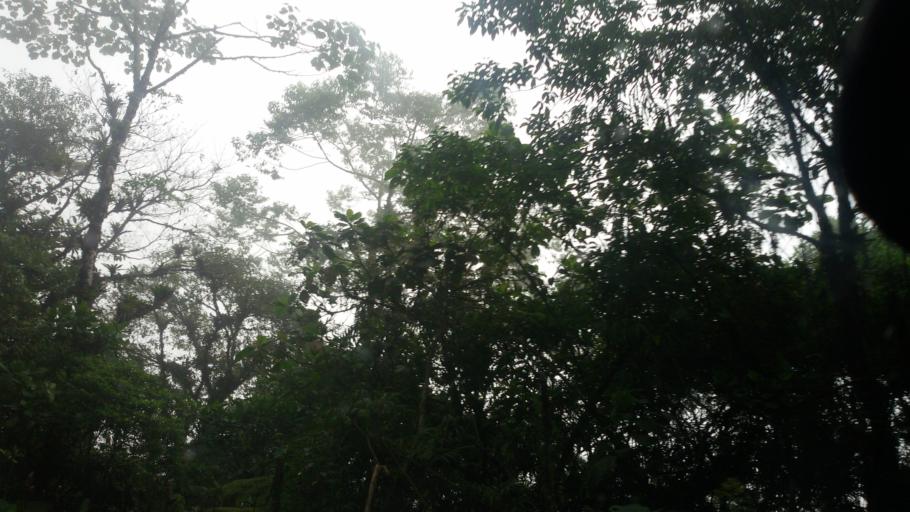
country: CR
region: San Jose
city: Ipis
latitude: 10.0221
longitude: -83.9465
